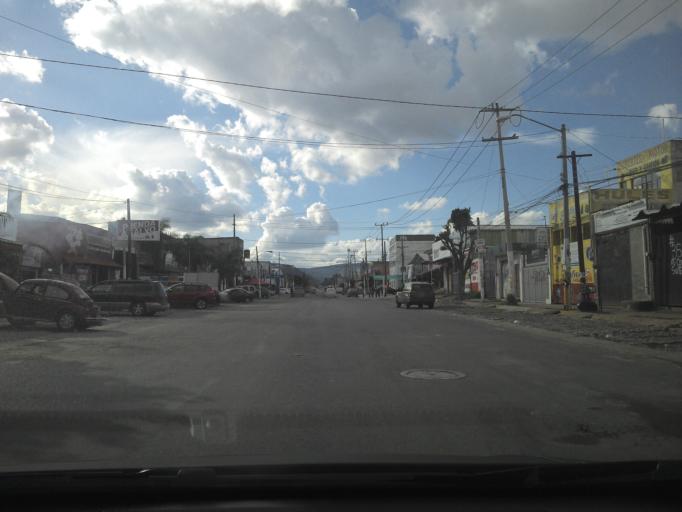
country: MX
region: Jalisco
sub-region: Tlajomulco de Zuniga
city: La Tijera
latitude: 20.6138
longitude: -103.4346
